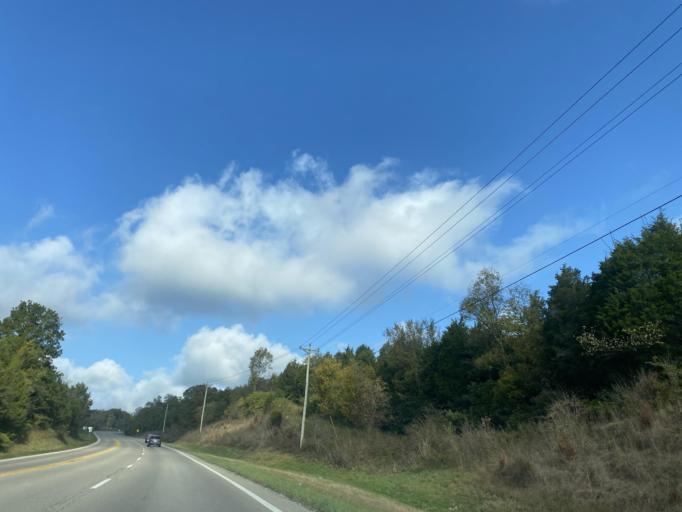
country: US
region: Kentucky
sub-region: Campbell County
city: Claryville
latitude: 38.8207
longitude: -84.3607
